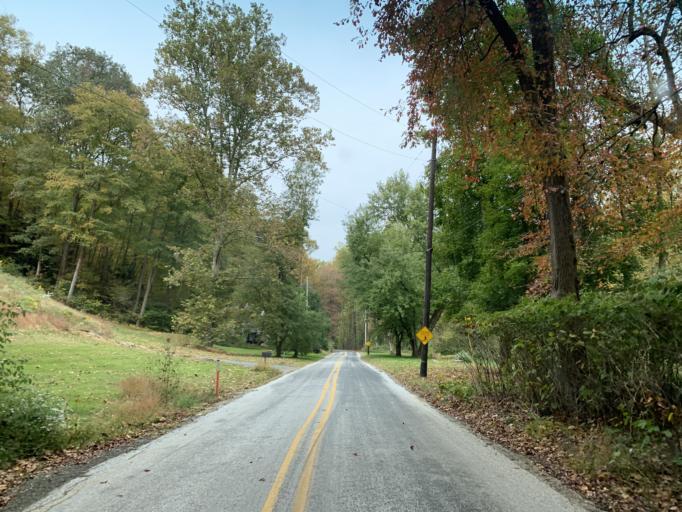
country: US
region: Pennsylvania
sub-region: York County
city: Susquehanna Trails
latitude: 39.7886
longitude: -76.4109
